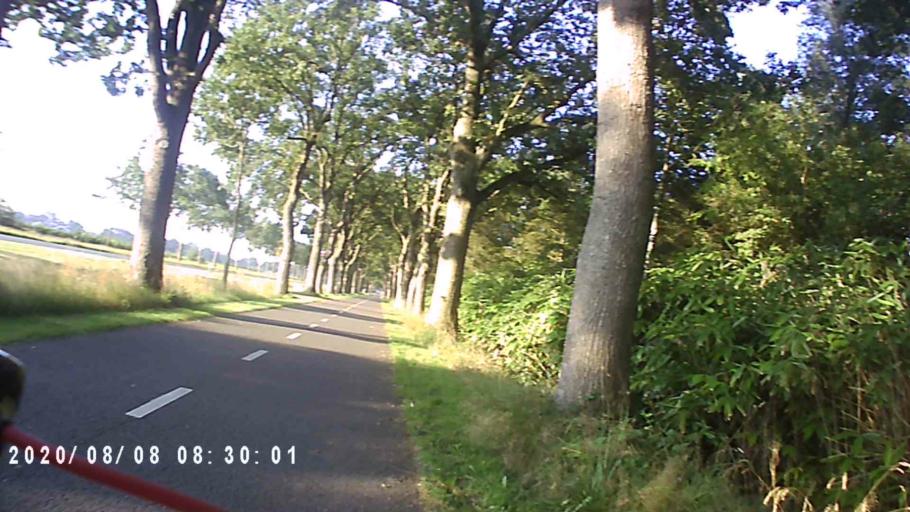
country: NL
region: Groningen
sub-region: Gemeente Leek
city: Leek
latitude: 53.0803
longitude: 6.3358
